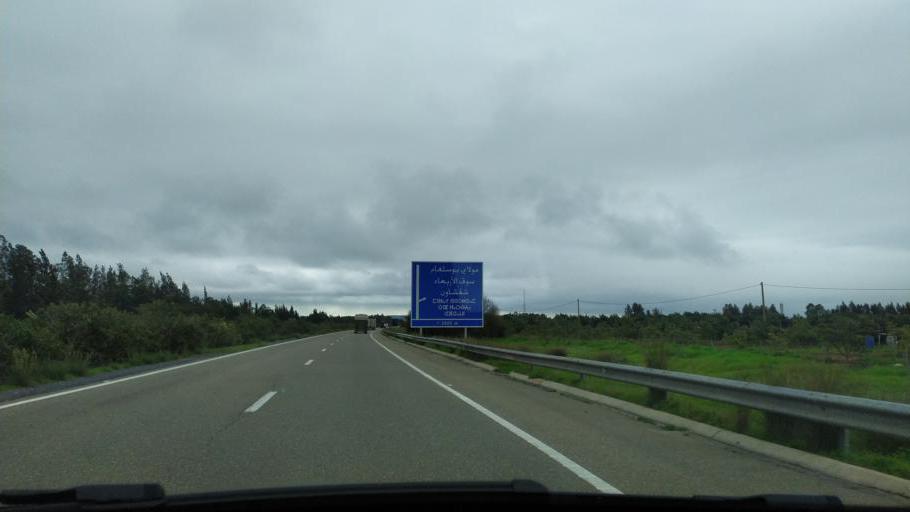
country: MA
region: Gharb-Chrarda-Beni Hssen
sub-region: Kenitra Province
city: Lalla Mimouna
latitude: 34.8856
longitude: -6.2107
